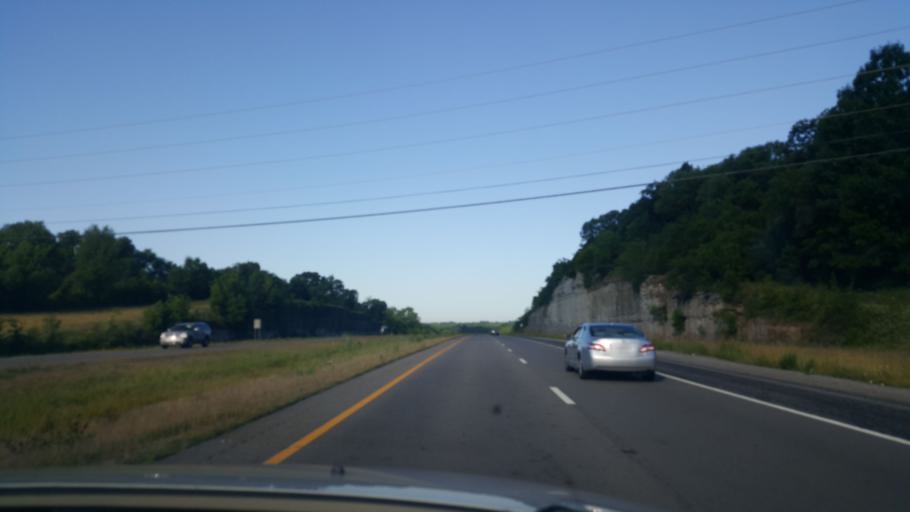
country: US
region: Tennessee
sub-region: Maury County
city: Columbia
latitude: 35.6280
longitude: -87.1060
